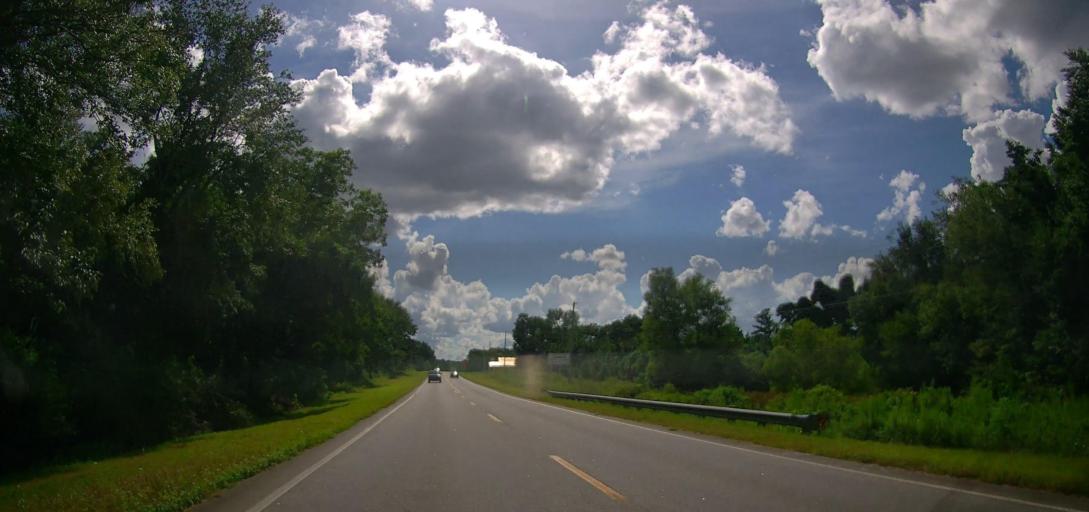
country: US
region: Alabama
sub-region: Lee County
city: Opelika
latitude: 32.4407
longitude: -85.3017
